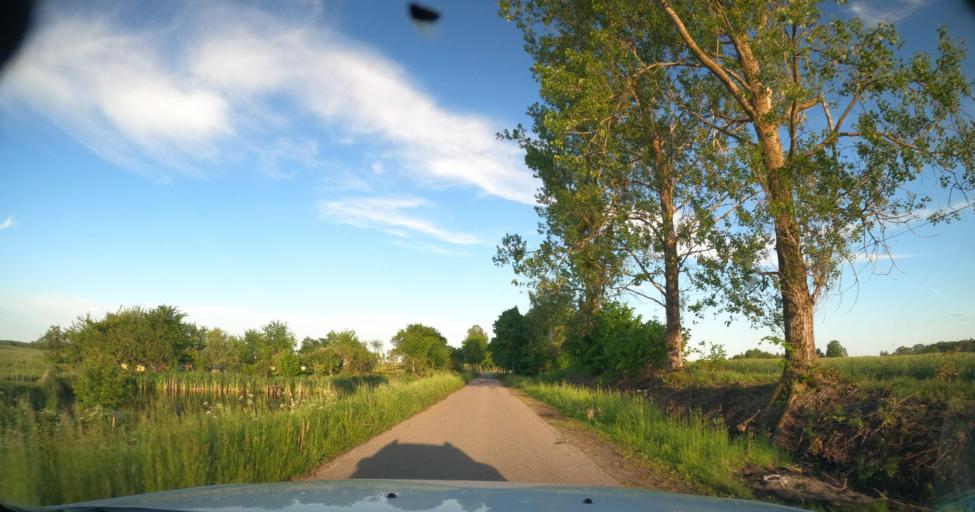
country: PL
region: Warmian-Masurian Voivodeship
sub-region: Powiat lidzbarski
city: Orneta
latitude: 54.1740
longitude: 20.1606
